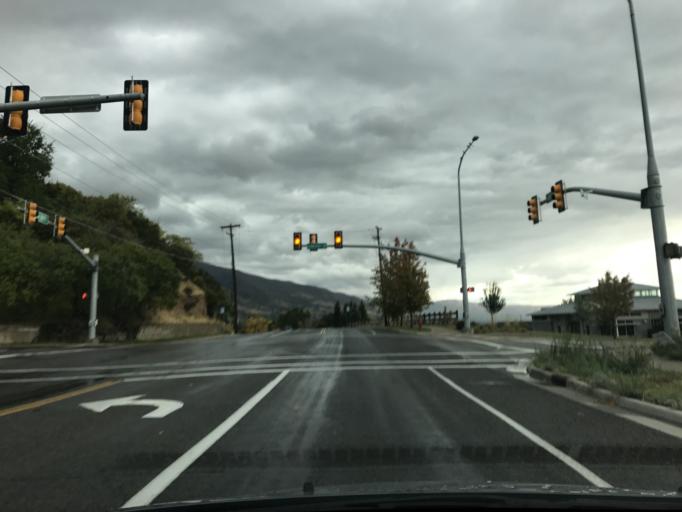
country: US
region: Utah
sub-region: Davis County
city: Fruit Heights
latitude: 41.0085
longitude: -111.9082
